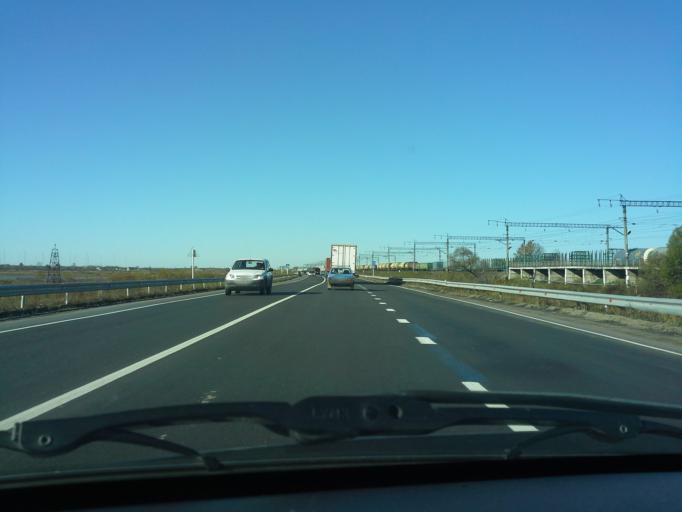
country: RU
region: Jewish Autonomous Oblast
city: Priamurskiy
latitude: 48.5268
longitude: 134.9453
